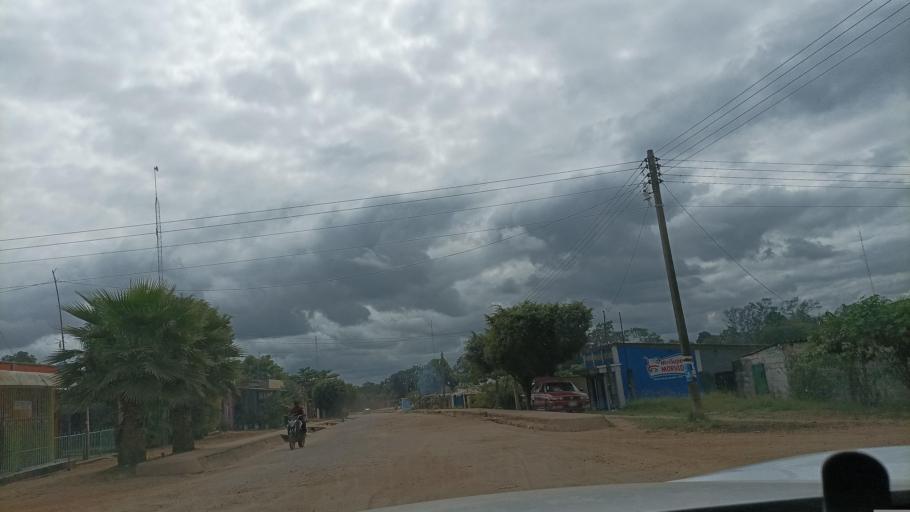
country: MX
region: Veracruz
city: Texistepec
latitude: 17.9611
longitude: -94.8143
